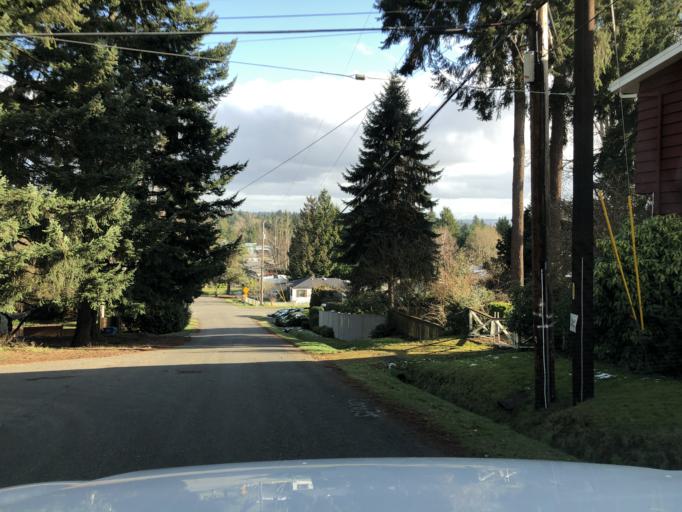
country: US
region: Washington
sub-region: King County
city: Lake Forest Park
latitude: 47.7139
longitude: -122.3030
